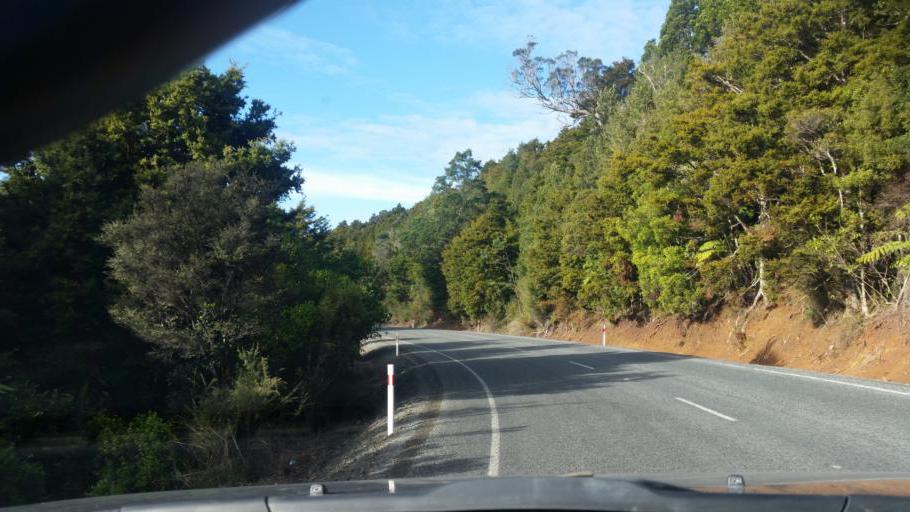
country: NZ
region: Northland
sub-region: Kaipara District
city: Dargaville
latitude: -35.7399
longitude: 173.6643
